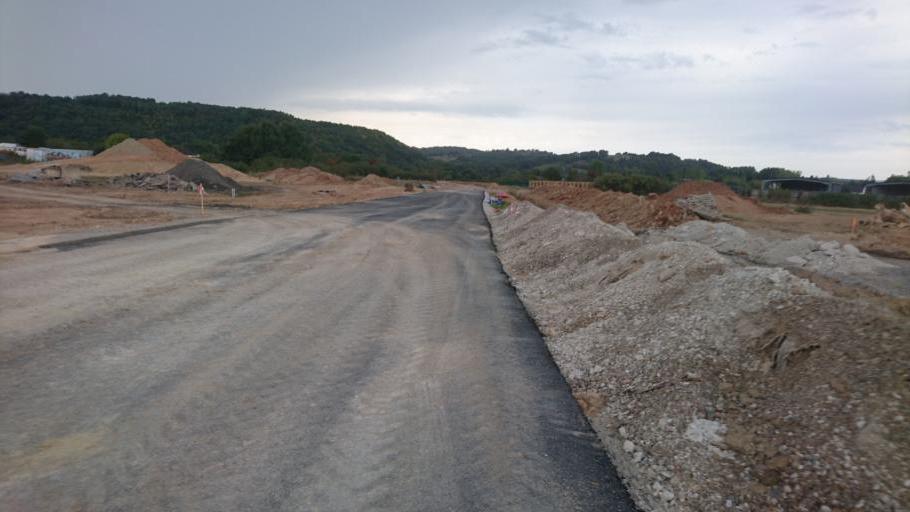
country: FR
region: Limousin
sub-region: Departement de la Correze
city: Saint-Pantaleon-de-Larche
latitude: 45.1551
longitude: 1.4666
